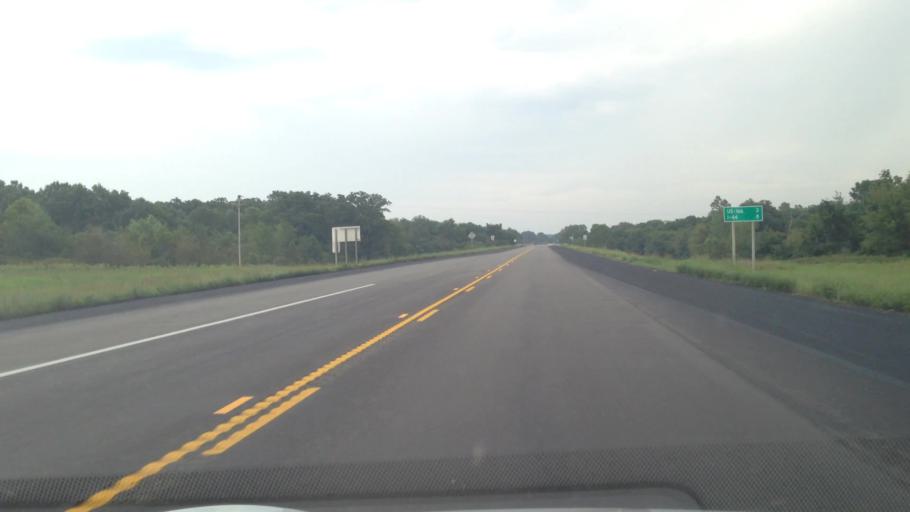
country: US
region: Kansas
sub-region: Cherokee County
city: Baxter Springs
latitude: 37.0551
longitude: -94.7343
